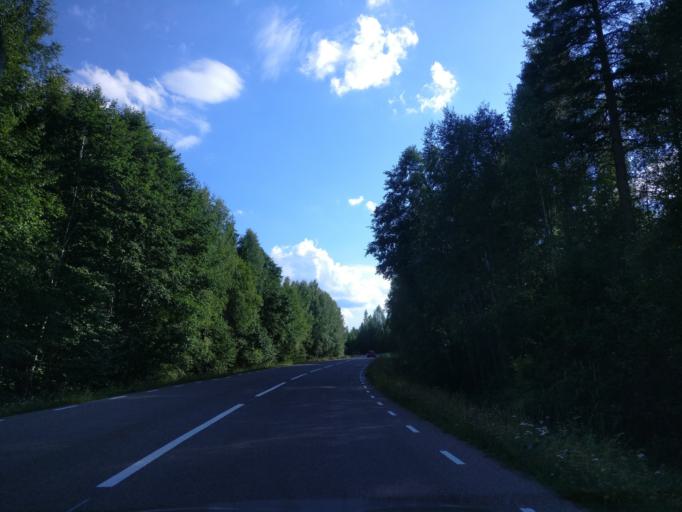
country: SE
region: Dalarna
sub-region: Ludvika Kommun
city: Ludvika
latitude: 60.2968
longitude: 15.2178
